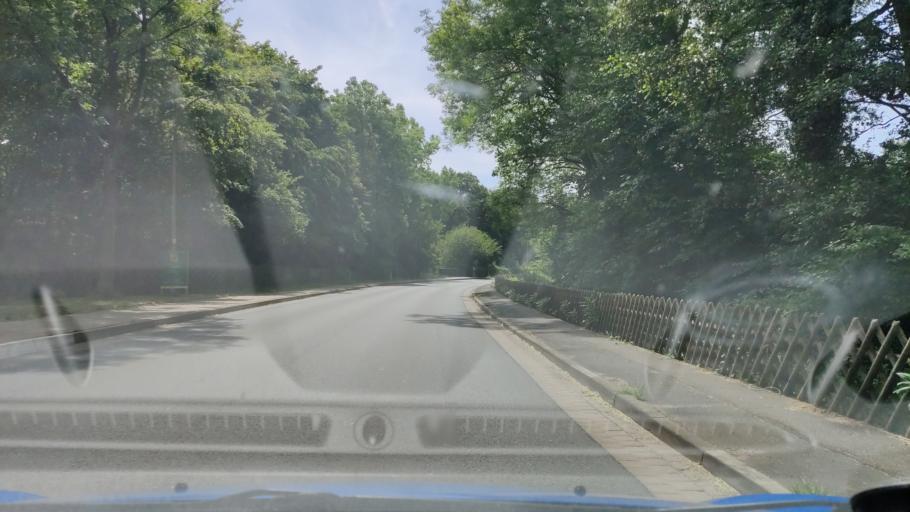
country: DE
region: Lower Saxony
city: Neustadt am Rubenberge
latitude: 52.5582
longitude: 9.4881
